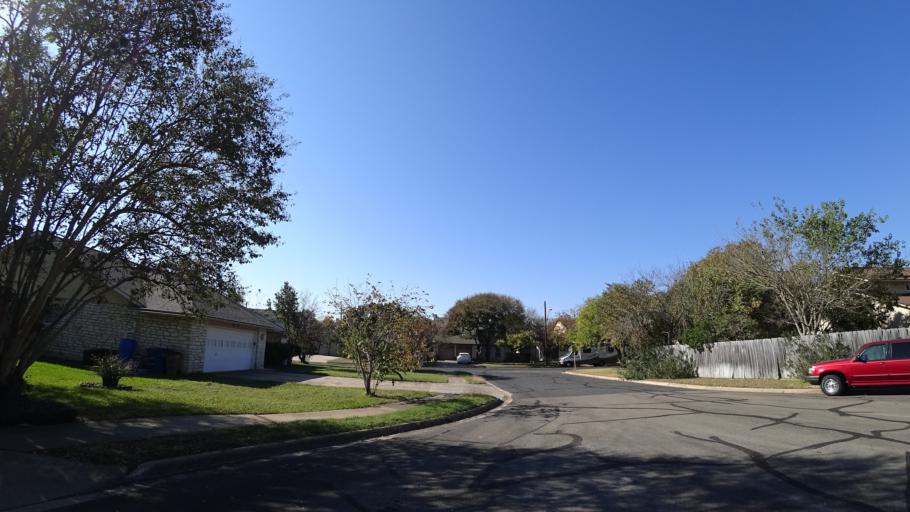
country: US
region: Texas
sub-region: Travis County
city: Barton Creek
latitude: 30.2289
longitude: -97.8510
